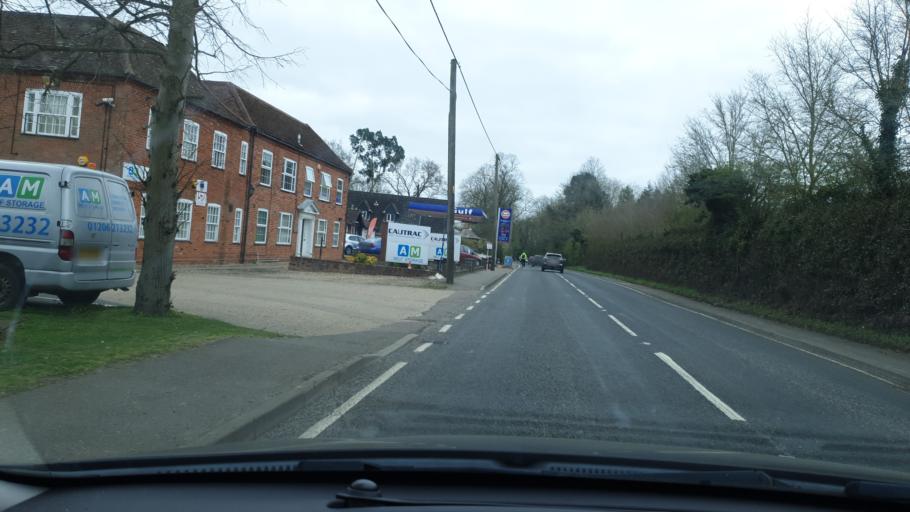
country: GB
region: England
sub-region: Essex
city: Great Horkesley
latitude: 51.9338
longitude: 0.8762
